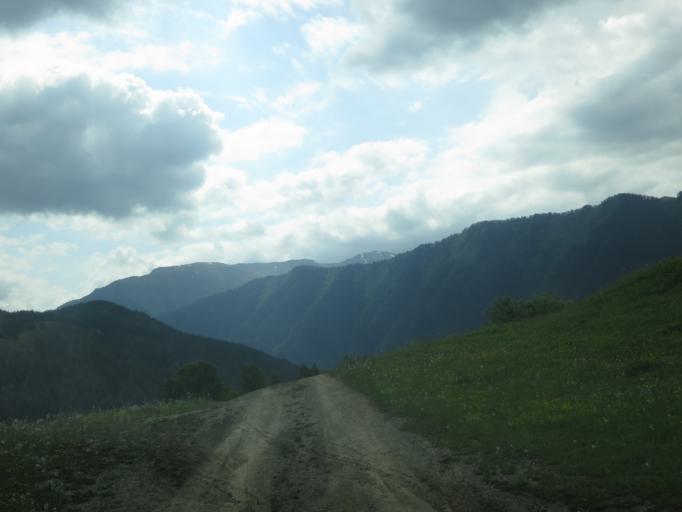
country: RU
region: Chechnya
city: Itum-Kali
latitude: 42.3675
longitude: 45.6394
